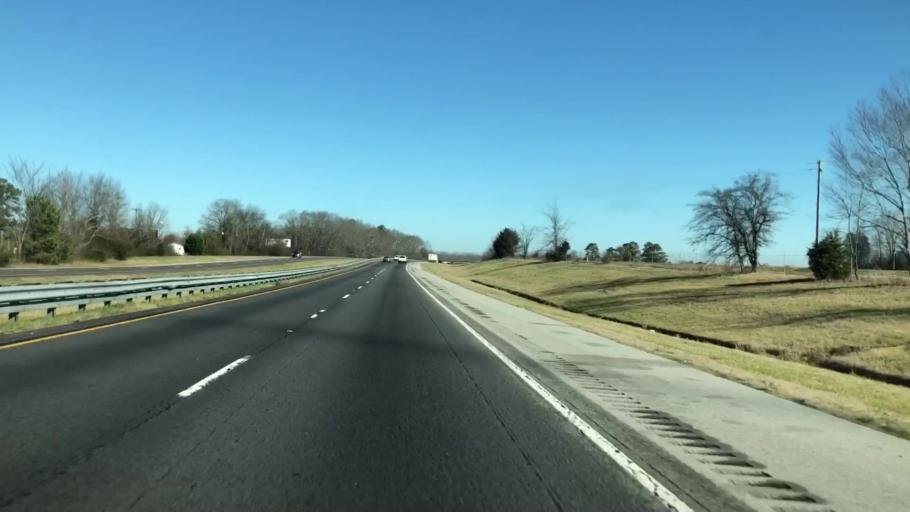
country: US
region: Alabama
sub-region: Limestone County
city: Athens
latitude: 34.8853
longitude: -86.9177
